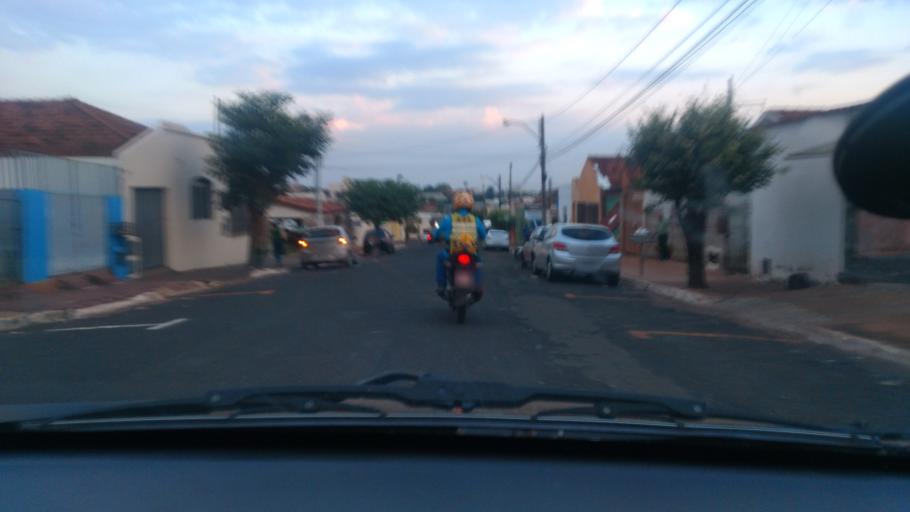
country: BR
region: Goias
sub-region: Santa Helena De Goias
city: Santa Helena de Goias
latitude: -17.7943
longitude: -50.9274
